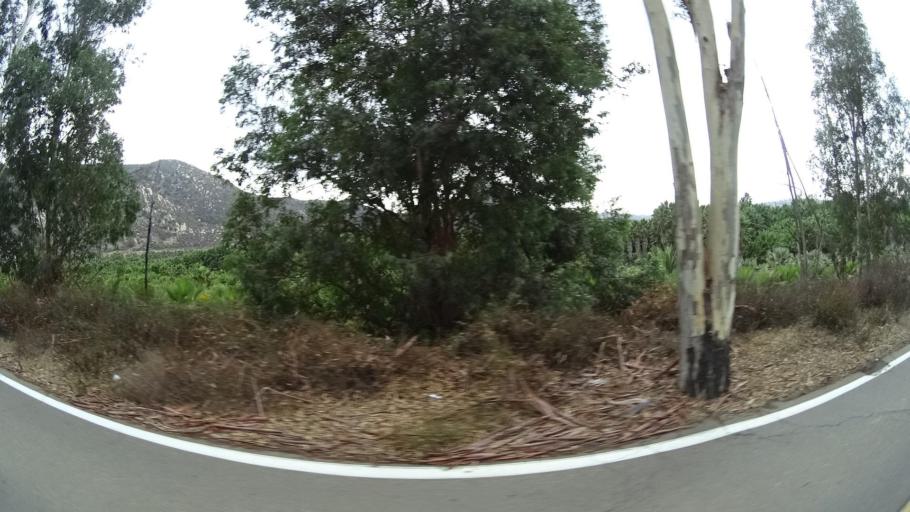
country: US
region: California
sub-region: San Diego County
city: San Pasqual
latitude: 33.0620
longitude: -117.0283
